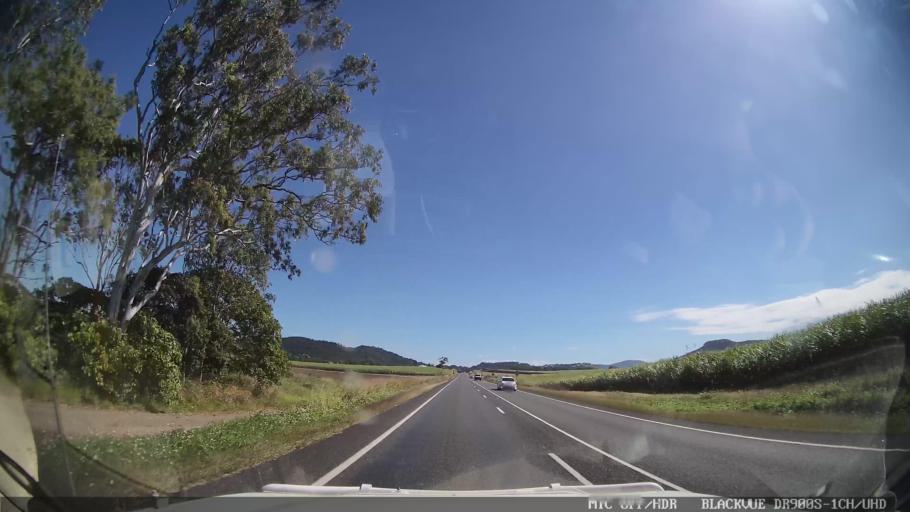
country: AU
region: Queensland
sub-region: Mackay
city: Walkerston
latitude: -21.0906
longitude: 149.0511
